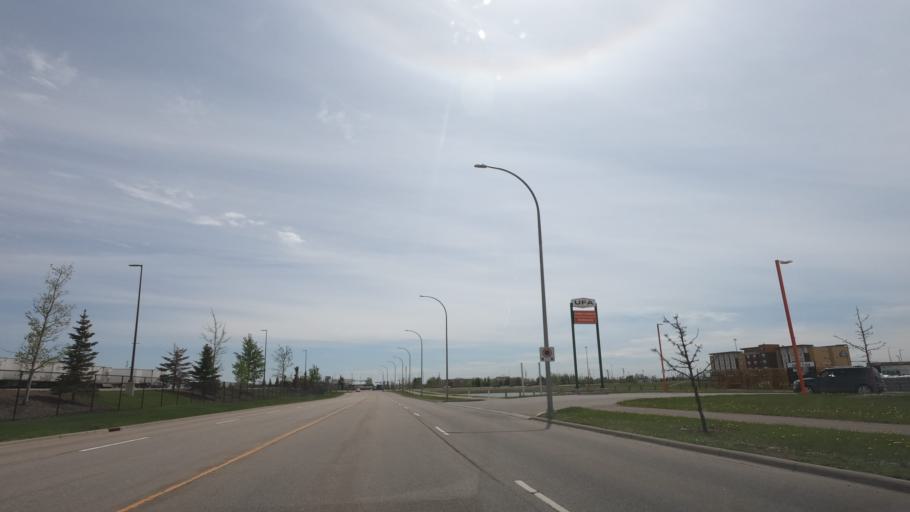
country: CA
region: Alberta
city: Airdrie
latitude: 51.3030
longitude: -113.9949
